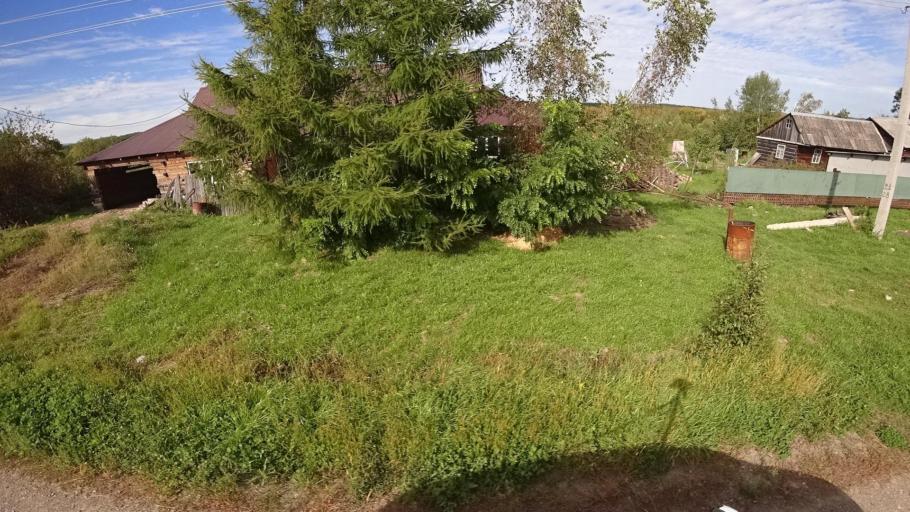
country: RU
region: Primorskiy
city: Dostoyevka
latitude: 44.3272
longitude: 133.4959
